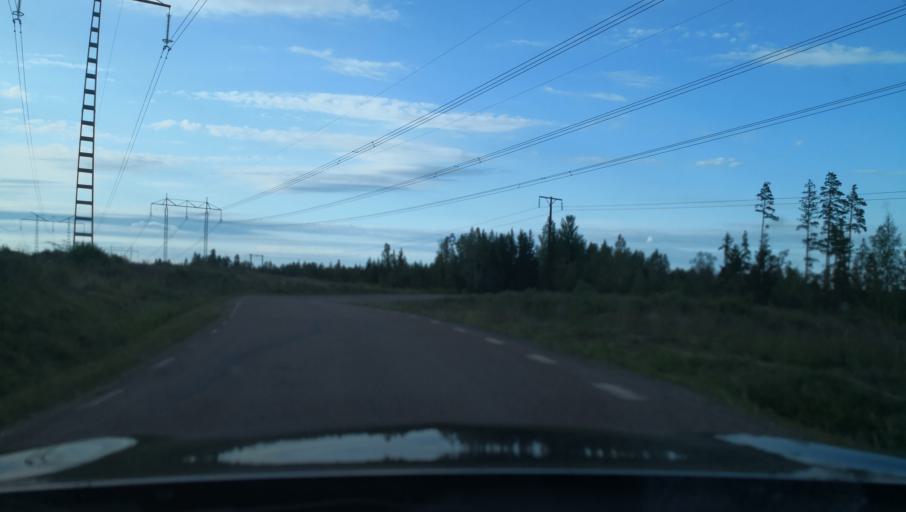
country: SE
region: Dalarna
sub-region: Ludvika Kommun
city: Ludvika
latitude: 60.1099
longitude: 15.2673
